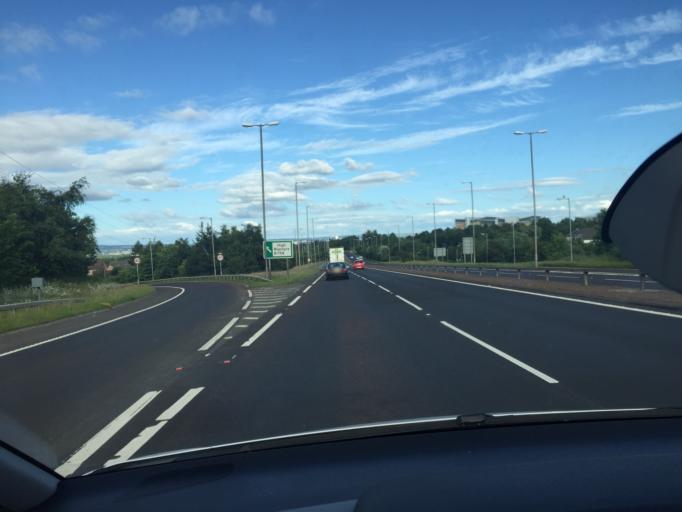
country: GB
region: Scotland
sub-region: South Lanarkshire
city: High Blantyre
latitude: 55.7830
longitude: -4.1102
